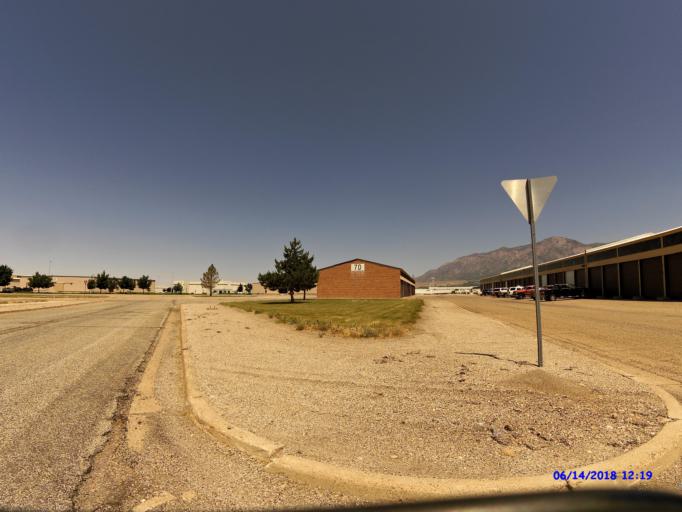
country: US
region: Utah
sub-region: Weber County
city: Harrisville
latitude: 41.2617
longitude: -111.9970
